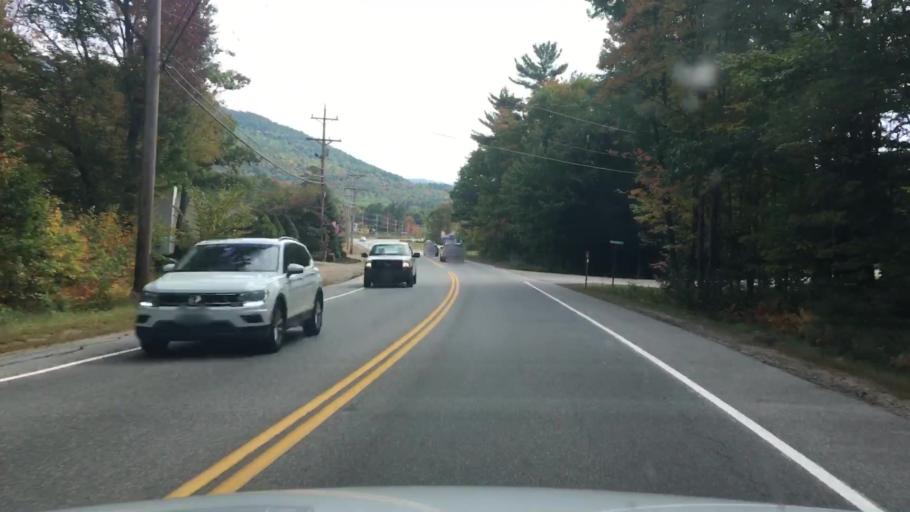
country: US
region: New Hampshire
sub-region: Carroll County
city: North Conway
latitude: 44.1091
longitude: -71.1639
